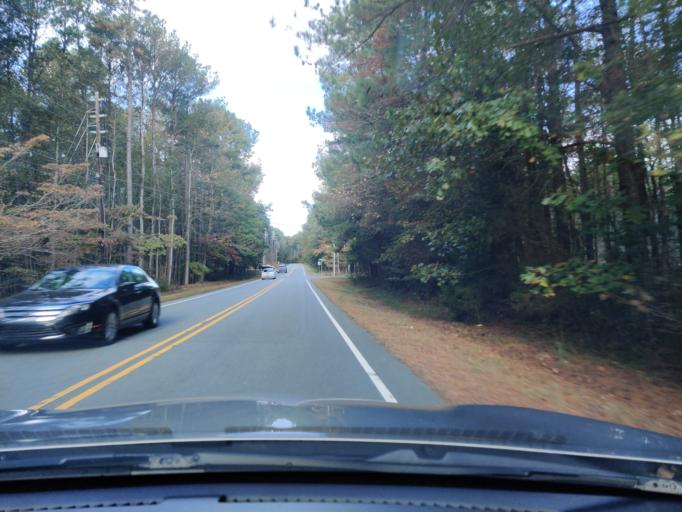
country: US
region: North Carolina
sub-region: Wake County
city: West Raleigh
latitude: 35.9189
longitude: -78.7152
